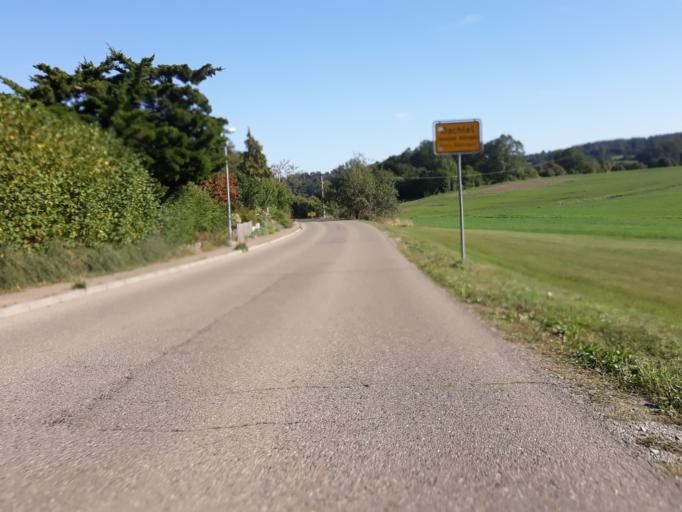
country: DE
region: Baden-Wuerttemberg
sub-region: Karlsruhe Region
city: Gechingen
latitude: 48.6849
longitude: 8.8457
